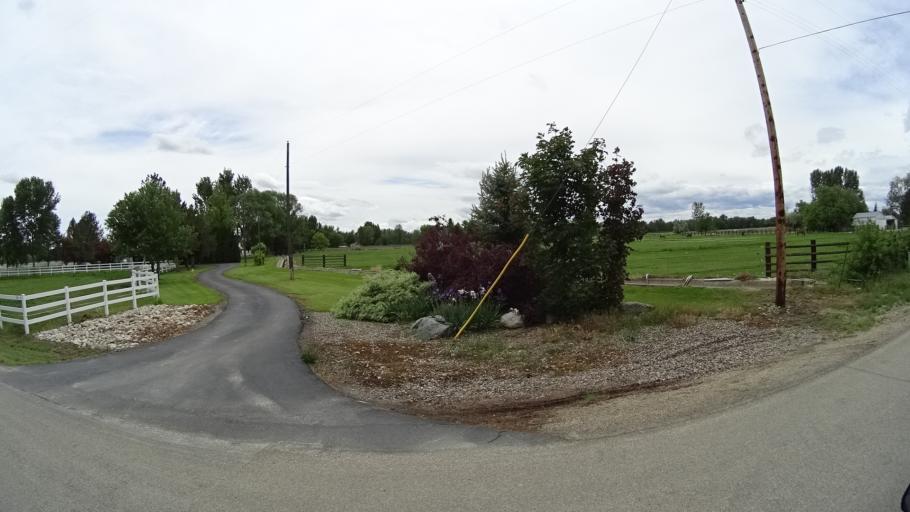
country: US
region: Idaho
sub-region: Ada County
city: Star
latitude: 43.6891
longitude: -116.4453
